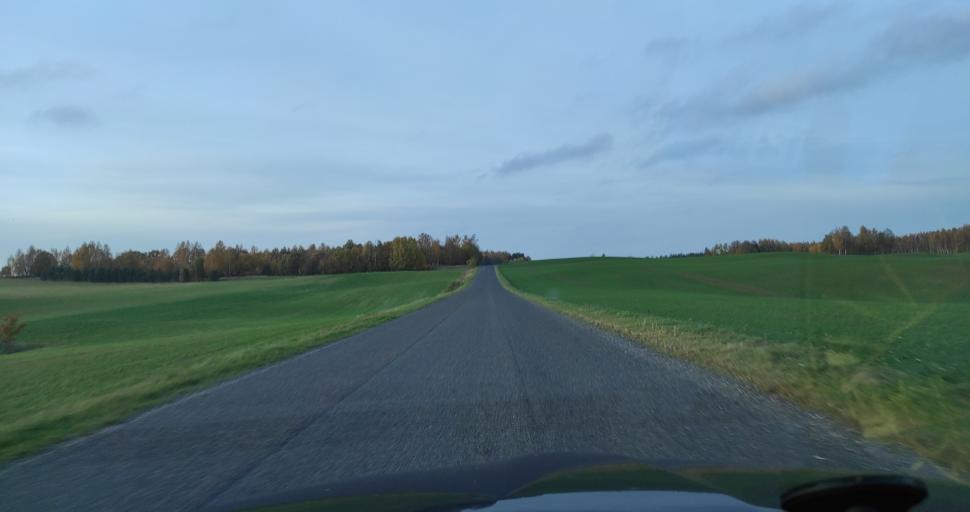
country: LV
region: Aizpute
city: Aizpute
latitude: 56.7034
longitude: 21.7944
